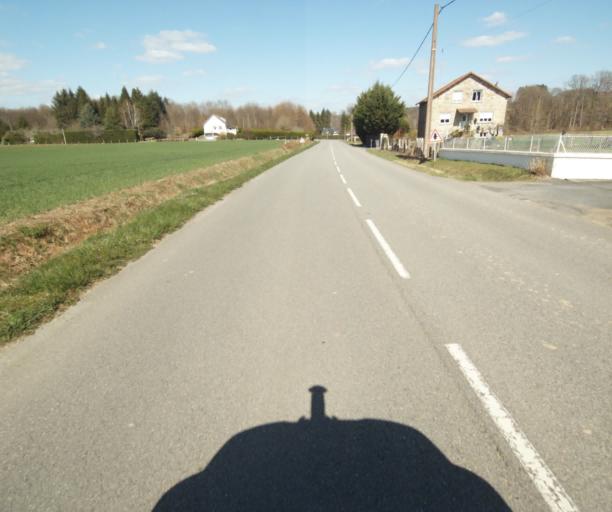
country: FR
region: Limousin
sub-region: Departement de la Correze
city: Saint-Mexant
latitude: 45.2884
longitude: 1.6663
